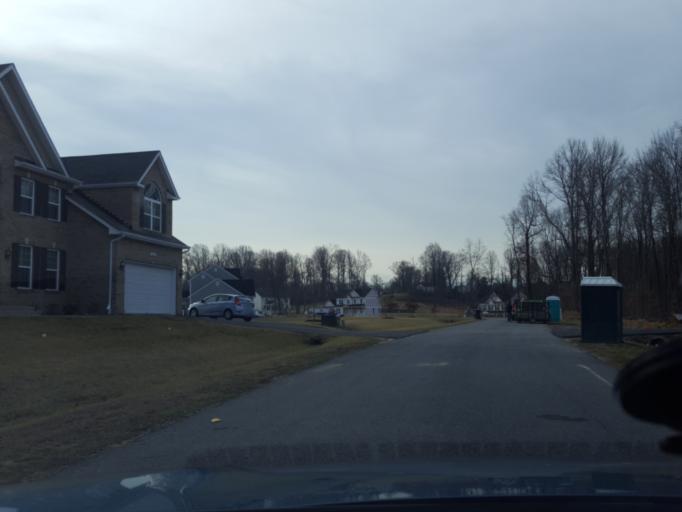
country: US
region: Maryland
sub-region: Calvert County
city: Chesapeake Beach
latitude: 38.6715
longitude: -76.5437
